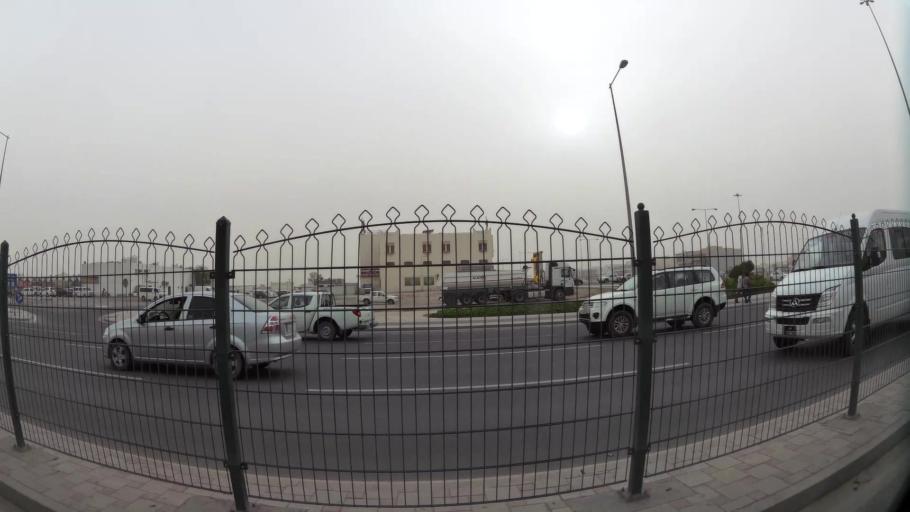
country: QA
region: Baladiyat ad Dawhah
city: Doha
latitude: 25.2485
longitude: 51.4723
